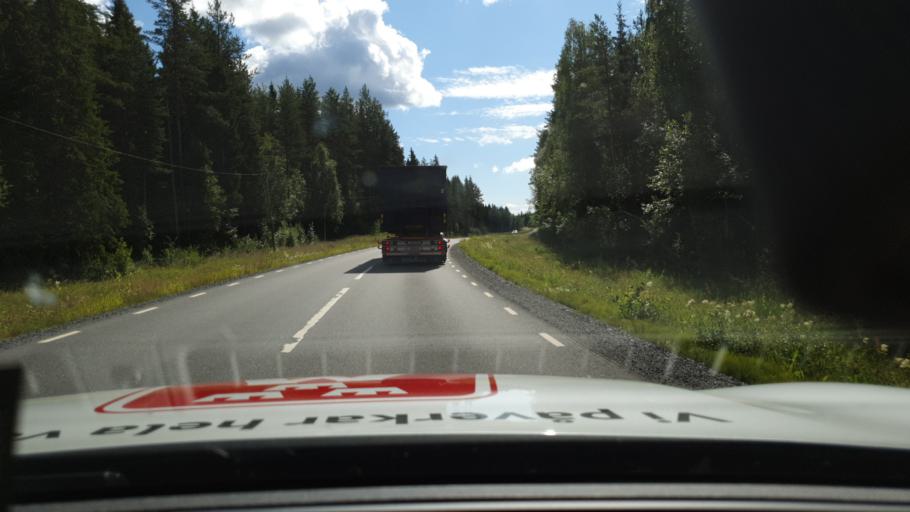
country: SE
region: Norrbotten
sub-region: Lulea Kommun
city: Ranea
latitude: 65.7884
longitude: 22.1537
